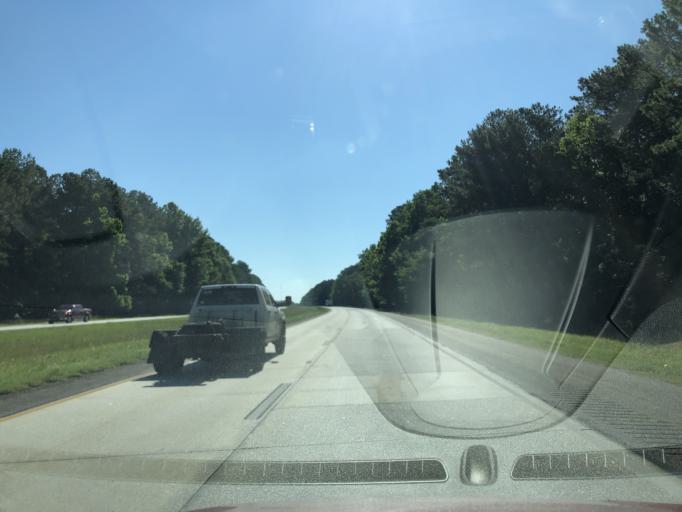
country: US
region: Georgia
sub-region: Warren County
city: Firing Range
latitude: 33.5006
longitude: -82.7832
